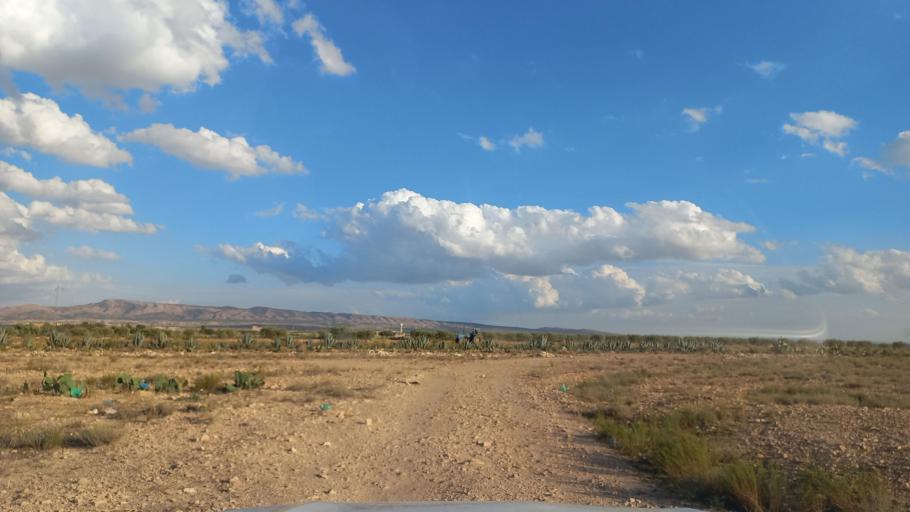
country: TN
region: Al Qasrayn
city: Sbiba
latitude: 35.3910
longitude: 9.0568
